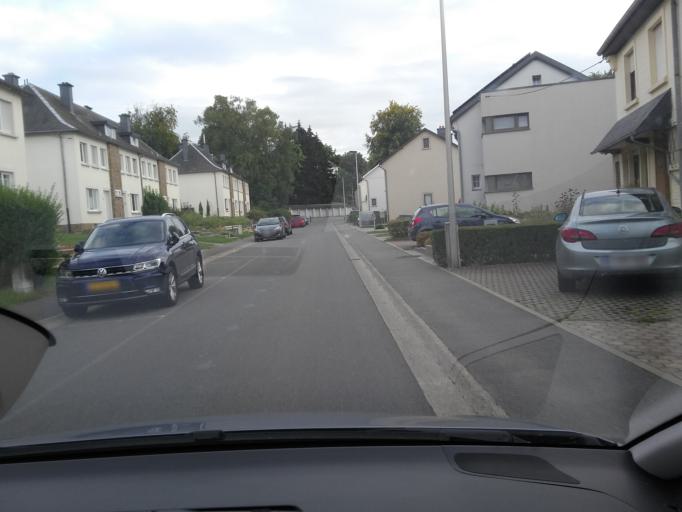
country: BE
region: Wallonia
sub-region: Province du Luxembourg
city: Arlon
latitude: 49.6901
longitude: 5.8017
